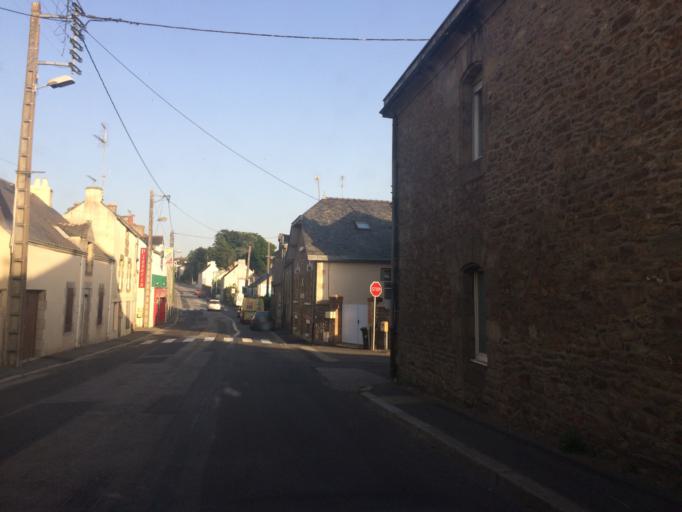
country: FR
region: Brittany
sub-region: Departement du Morbihan
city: Muzillac
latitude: 47.5545
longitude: -2.4900
